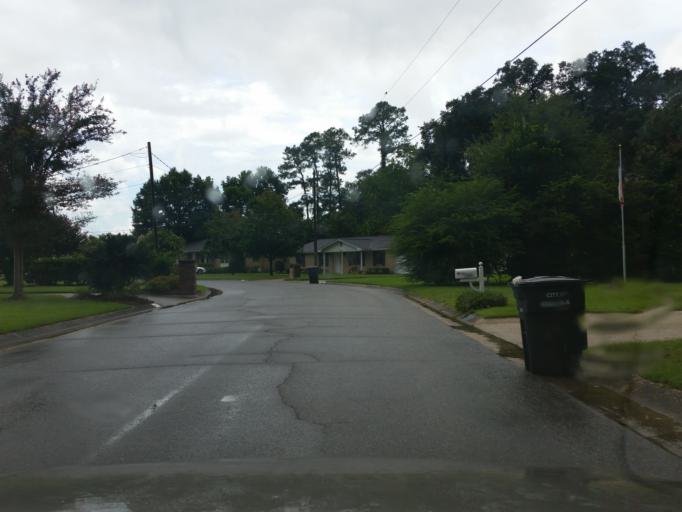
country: US
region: Florida
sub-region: Escambia County
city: Ferry Pass
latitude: 30.4891
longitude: -87.2162
